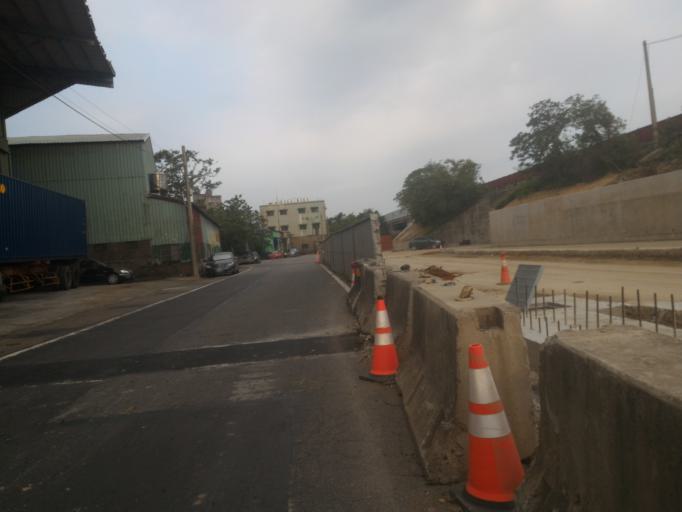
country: TW
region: Taiwan
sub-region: Taoyuan
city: Taoyuan
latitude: 24.9514
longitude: 121.3888
